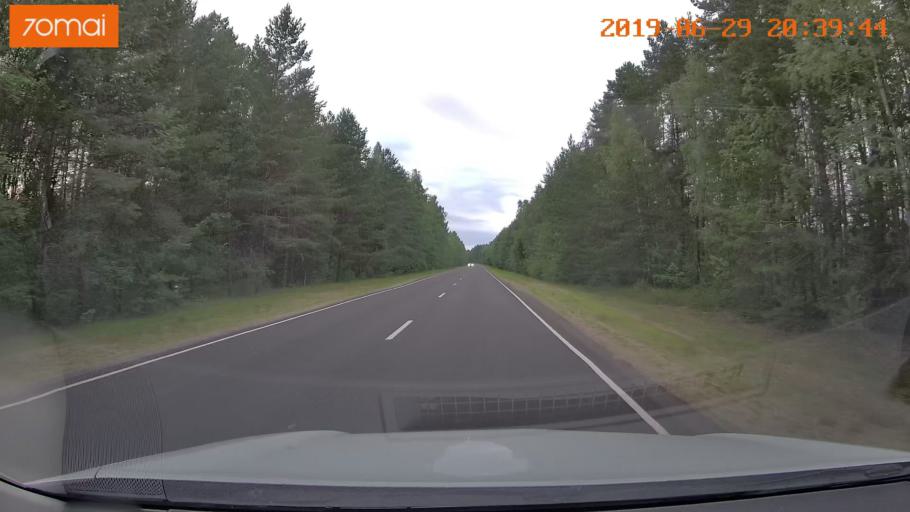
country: BY
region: Brest
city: Hantsavichy
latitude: 52.5661
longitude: 26.3599
